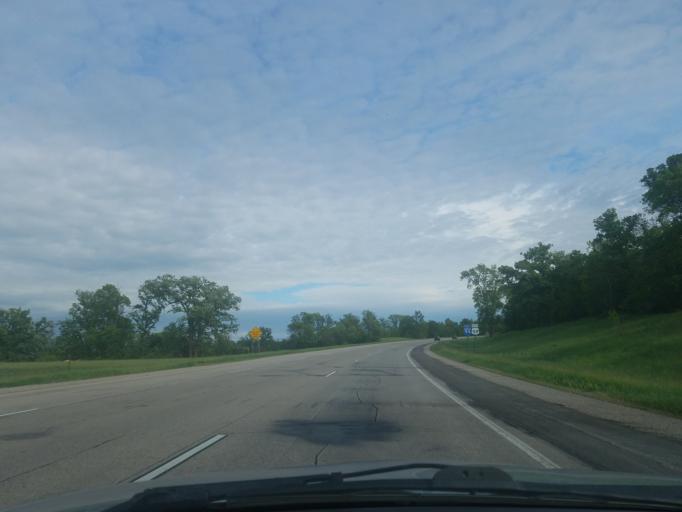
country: US
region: Minnesota
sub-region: Otter Tail County
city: Fergus Falls
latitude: 46.3338
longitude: -96.1254
